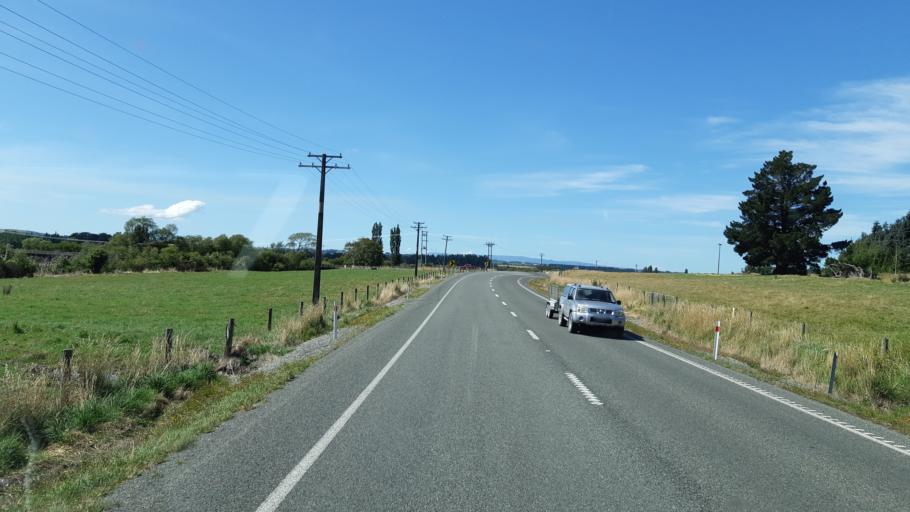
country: NZ
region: Southland
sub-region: Gore District
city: Gore
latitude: -46.0109
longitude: 168.8462
